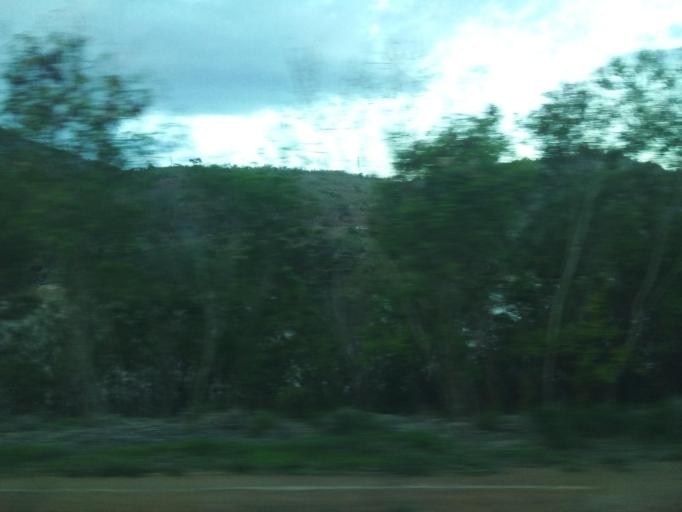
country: BR
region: Espirito Santo
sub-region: Baixo Guandu
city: Baixo Guandu
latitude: -19.5273
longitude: -40.8256
